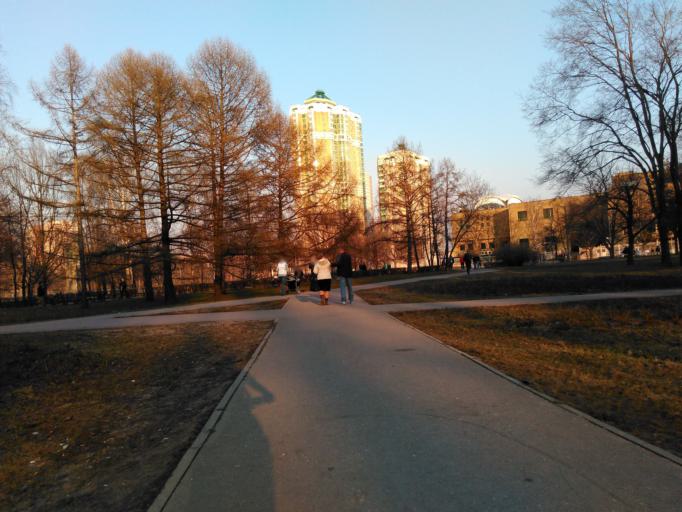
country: RU
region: Moscow
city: Ramenki
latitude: 55.6788
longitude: 37.5051
